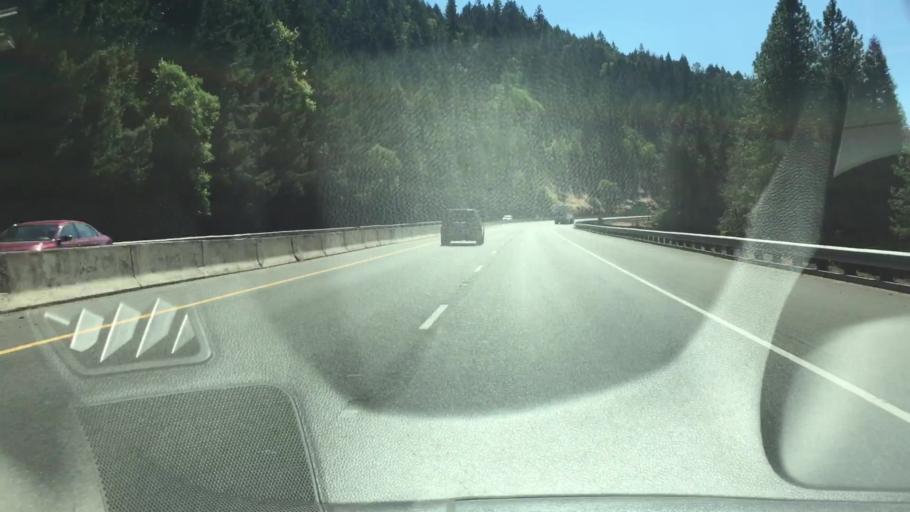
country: US
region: Oregon
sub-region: Josephine County
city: Merlin
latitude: 42.6833
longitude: -123.3870
